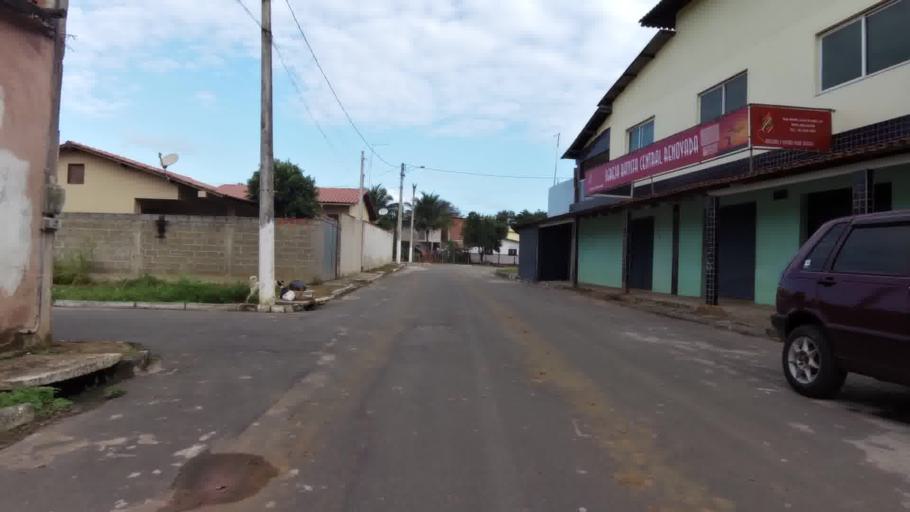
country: BR
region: Espirito Santo
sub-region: Piuma
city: Piuma
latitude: -20.7935
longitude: -40.6393
